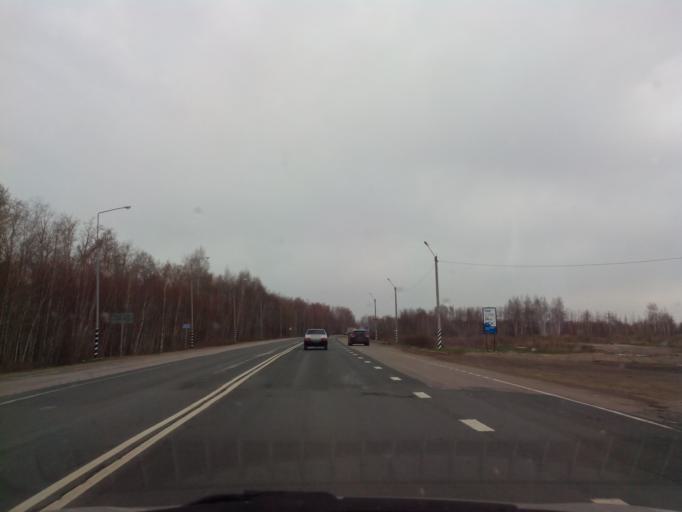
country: RU
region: Tambov
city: Pervomayskiy
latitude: 53.0875
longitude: 40.4020
